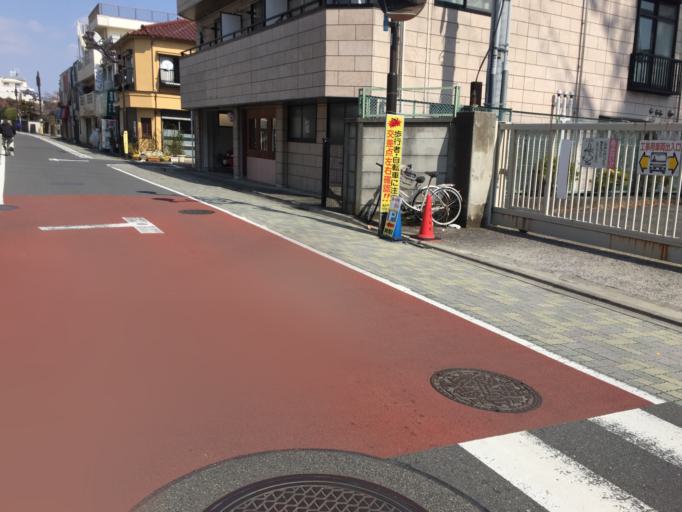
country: JP
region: Tokyo
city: Tokyo
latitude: 35.6805
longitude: 139.6463
